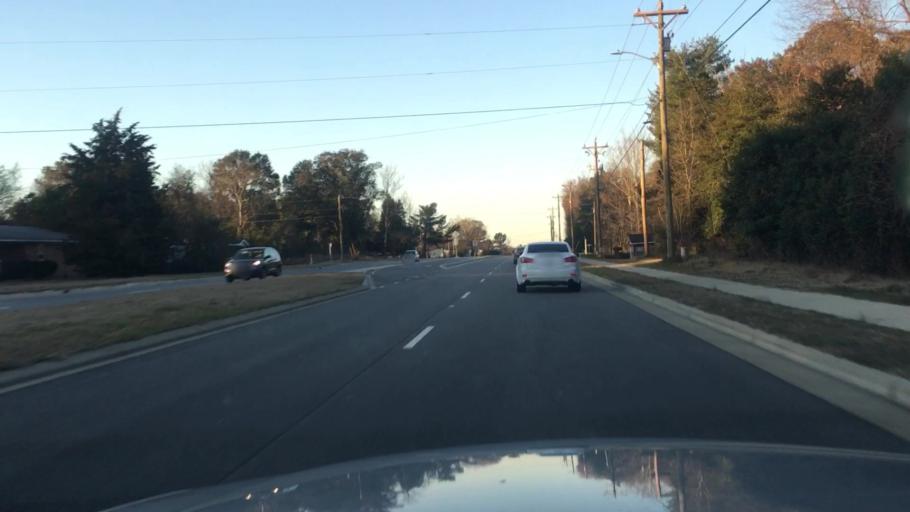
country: US
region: North Carolina
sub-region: Cumberland County
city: Hope Mills
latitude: 35.0051
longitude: -78.9225
